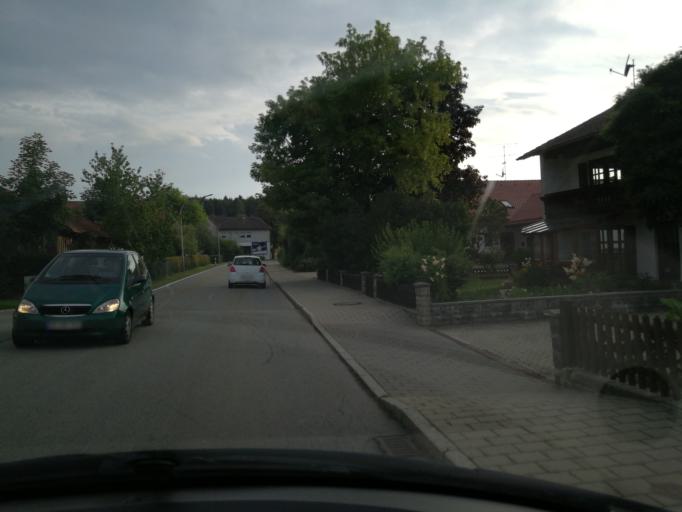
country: DE
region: Bavaria
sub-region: Lower Bavaria
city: Wiesenfelden
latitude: 49.0474
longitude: 12.5666
